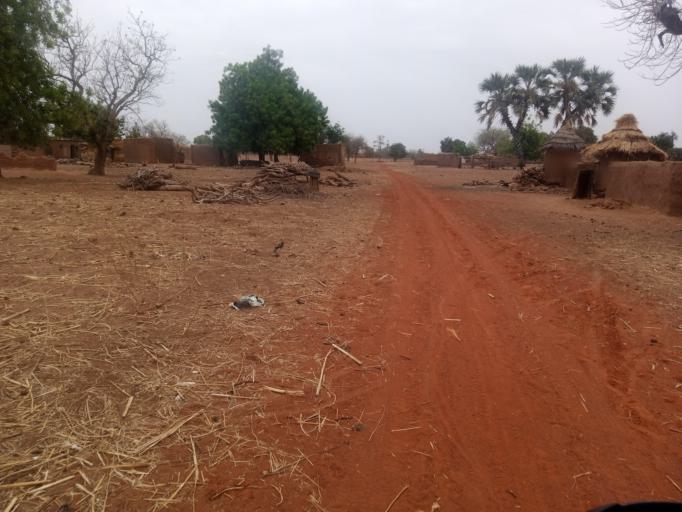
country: BF
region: Boucle du Mouhoun
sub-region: Province de la Kossi
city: Nouna
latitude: 12.8547
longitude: -4.0750
